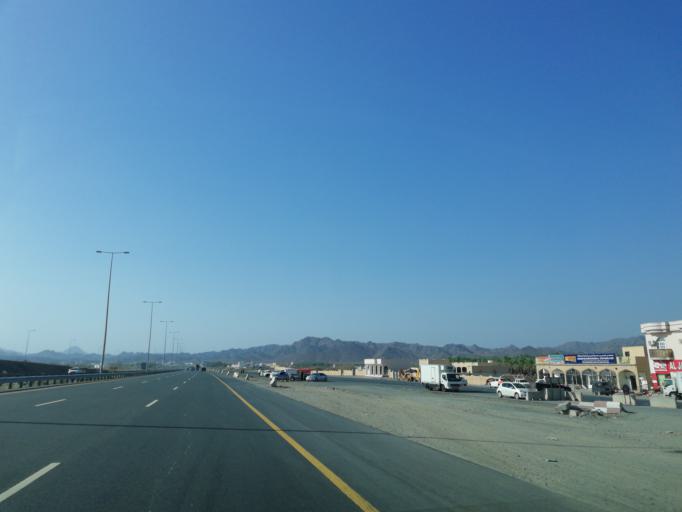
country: OM
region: Muhafazat ad Dakhiliyah
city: Sufalat Sama'il
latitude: 23.0410
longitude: 58.1994
